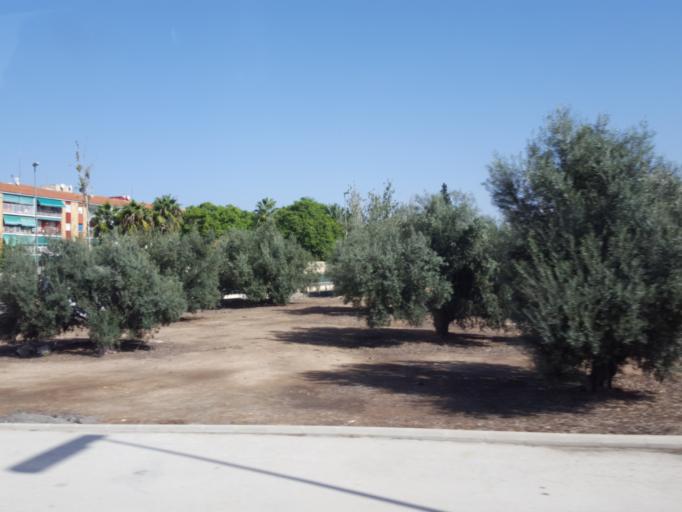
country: ES
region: Murcia
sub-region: Murcia
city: Murcia
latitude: 37.9908
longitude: -1.1454
